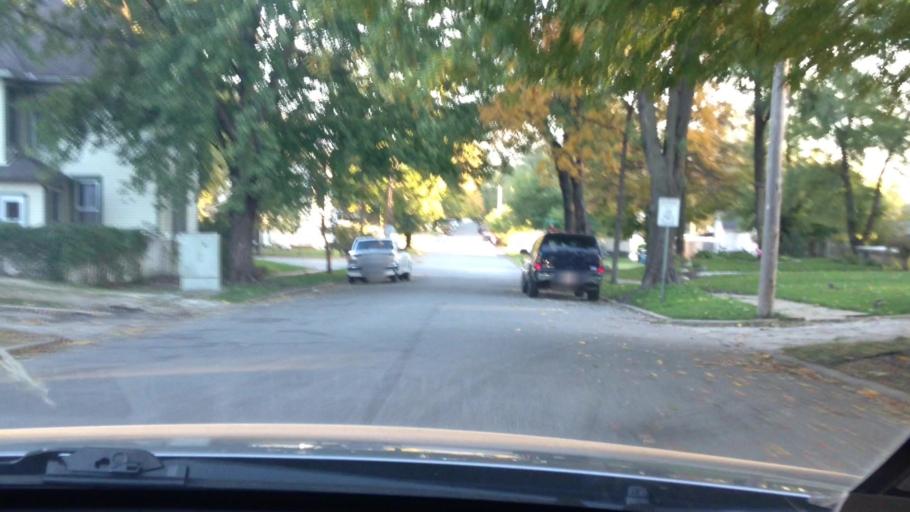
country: US
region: Kansas
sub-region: Leavenworth County
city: Leavenworth
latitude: 39.3236
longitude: -94.9182
